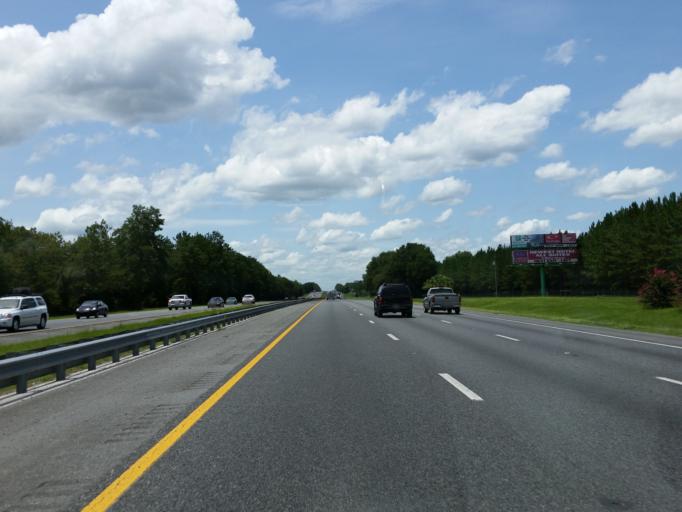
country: US
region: Florida
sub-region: Columbia County
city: Lake City
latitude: 30.1366
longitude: -82.6665
